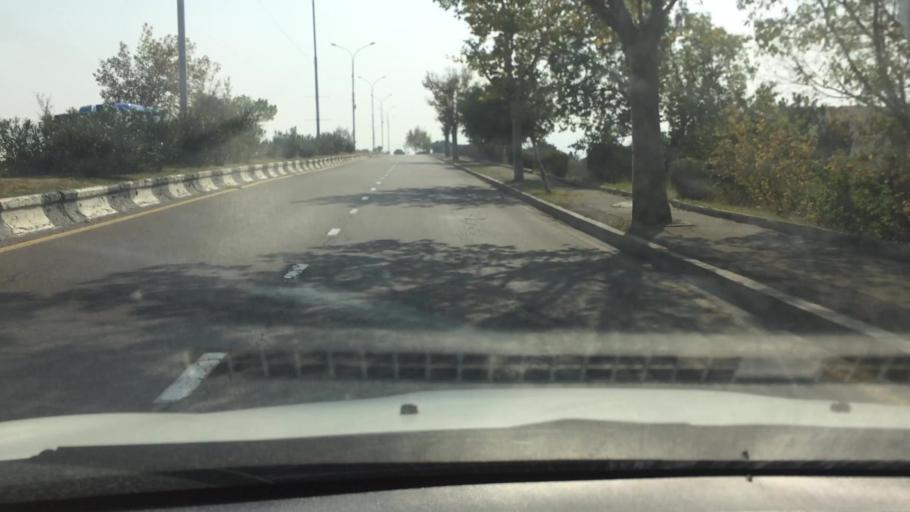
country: GE
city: Didi Lilo
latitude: 41.6880
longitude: 44.9530
